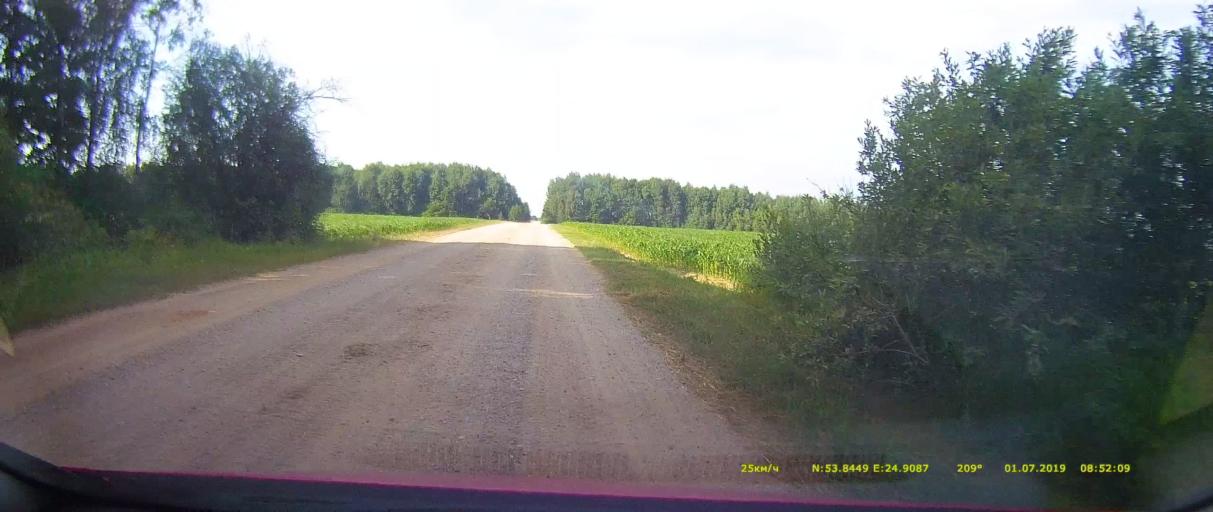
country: BY
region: Grodnenskaya
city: Shchuchin
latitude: 53.8450
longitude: 24.9088
